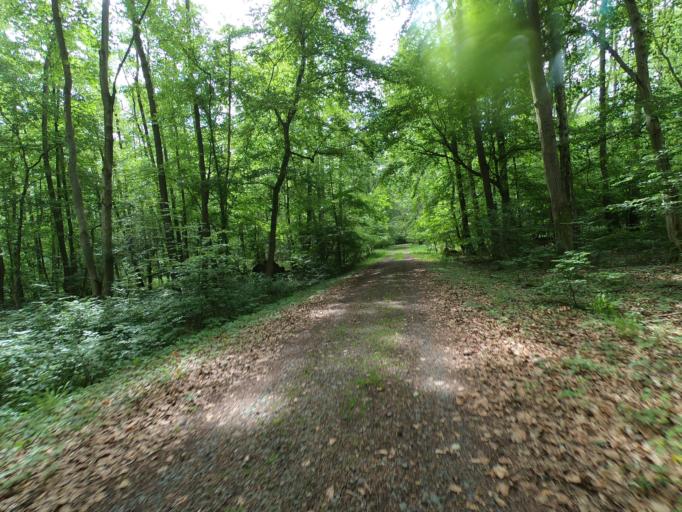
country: DE
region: Hesse
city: Morfelden-Walldorf
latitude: 49.9814
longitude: 8.5356
